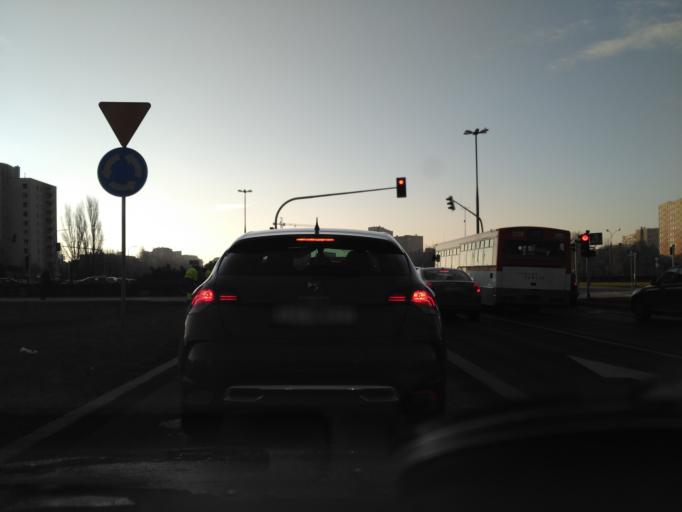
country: PL
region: Lublin Voivodeship
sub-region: Powiat lubelski
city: Lublin
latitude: 51.2631
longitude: 22.5514
